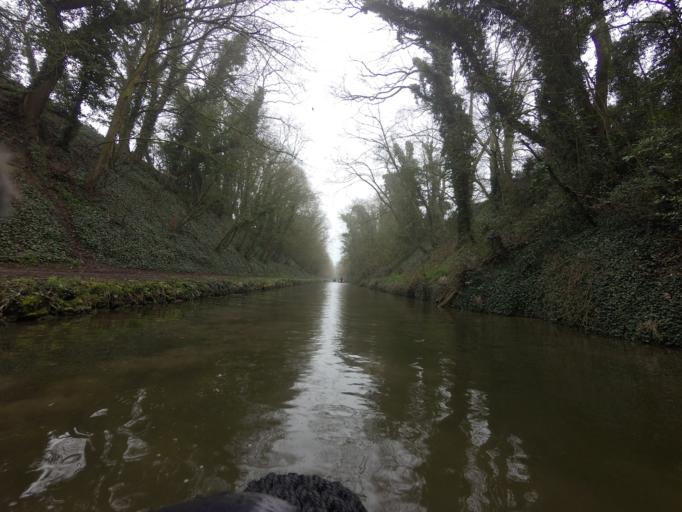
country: GB
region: England
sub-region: Hertfordshire
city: Tring
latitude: 51.8062
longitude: -0.6384
